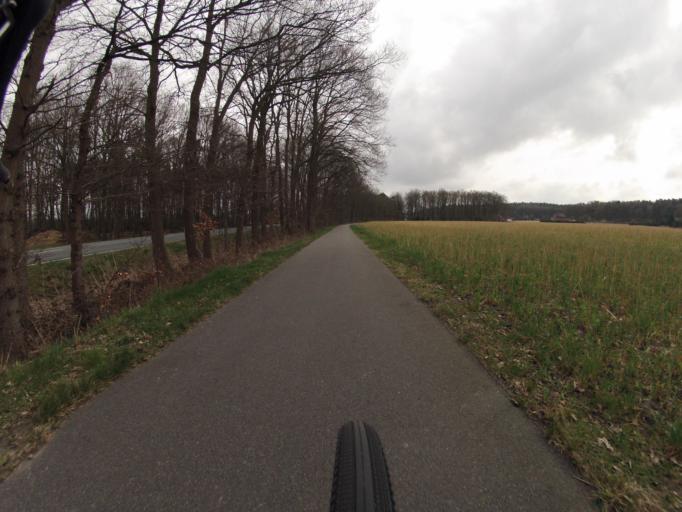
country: DE
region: North Rhine-Westphalia
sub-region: Regierungsbezirk Munster
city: Recke
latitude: 52.3417
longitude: 7.7173
